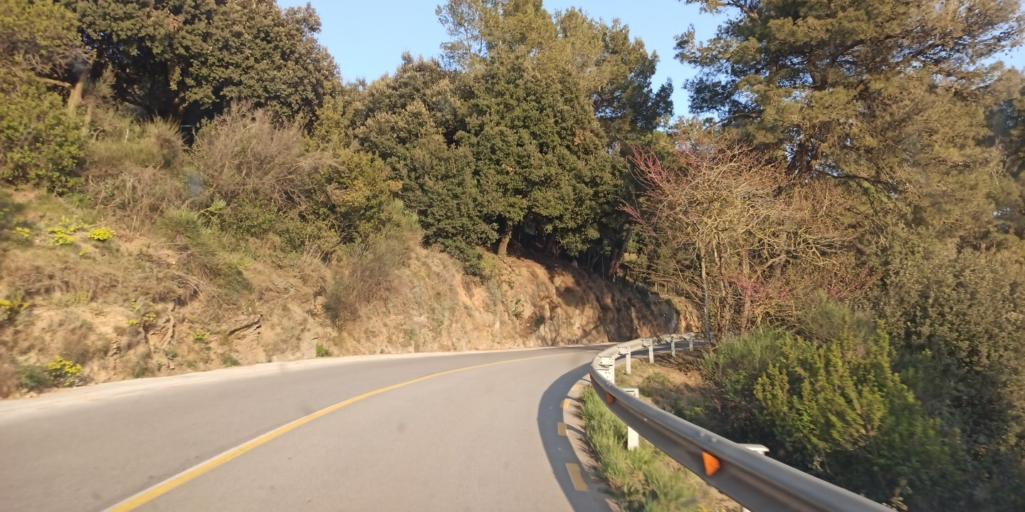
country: ES
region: Catalonia
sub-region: Provincia de Barcelona
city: Sant Just Desvern
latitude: 41.4082
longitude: 2.0925
